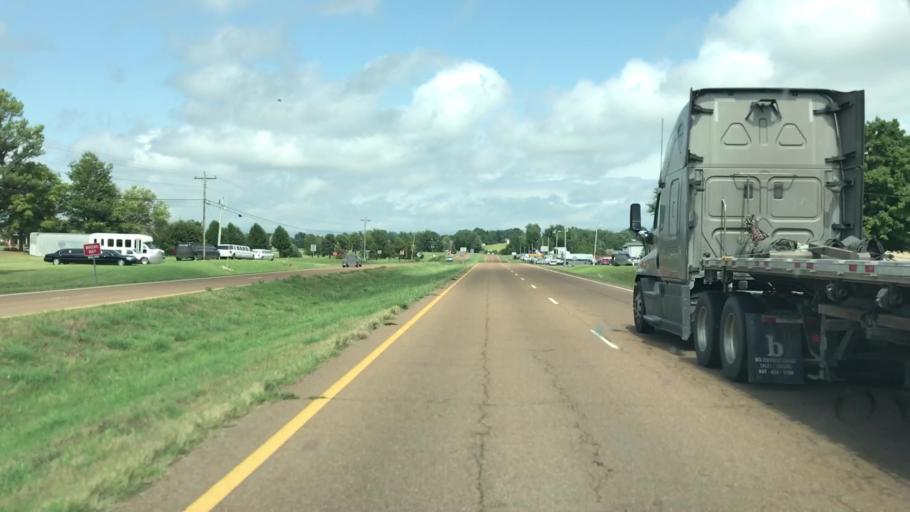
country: US
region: Tennessee
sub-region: Obion County
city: Englewood
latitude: 36.3494
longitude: -89.1460
